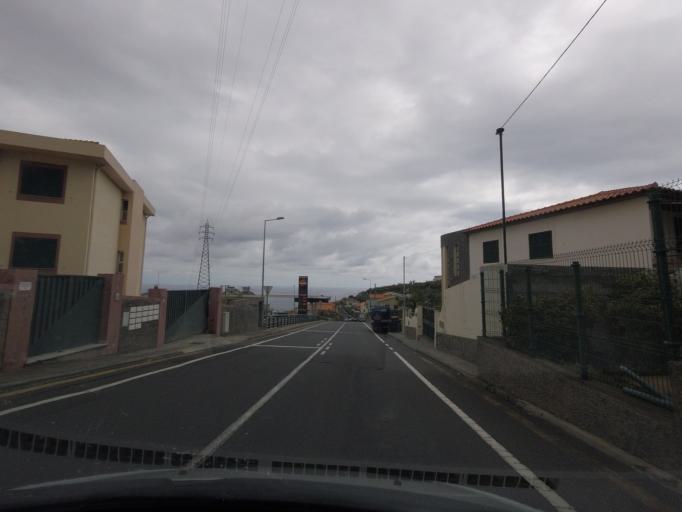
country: PT
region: Madeira
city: Camara de Lobos
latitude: 32.6557
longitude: -16.9663
